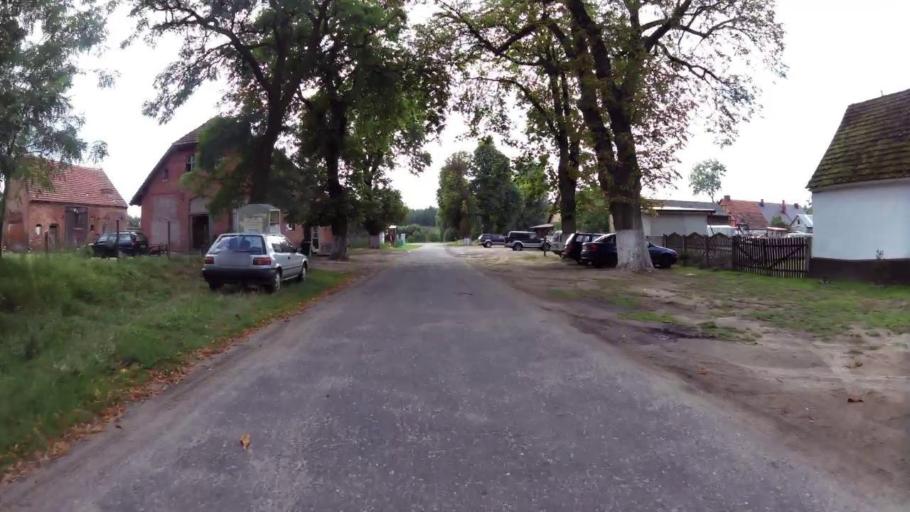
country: PL
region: West Pomeranian Voivodeship
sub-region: Powiat mysliborski
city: Debno
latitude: 52.7869
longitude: 14.6939
